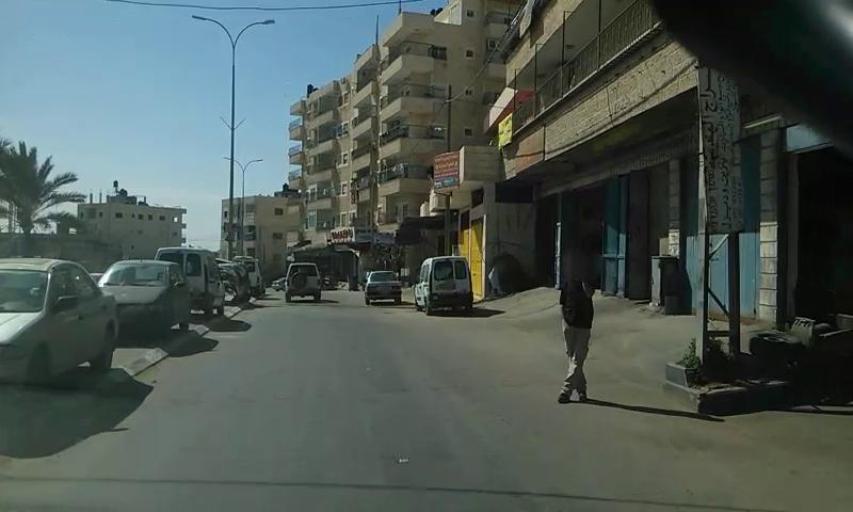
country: PS
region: West Bank
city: Al `Ayzariyah
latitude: 31.7613
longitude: 35.2813
